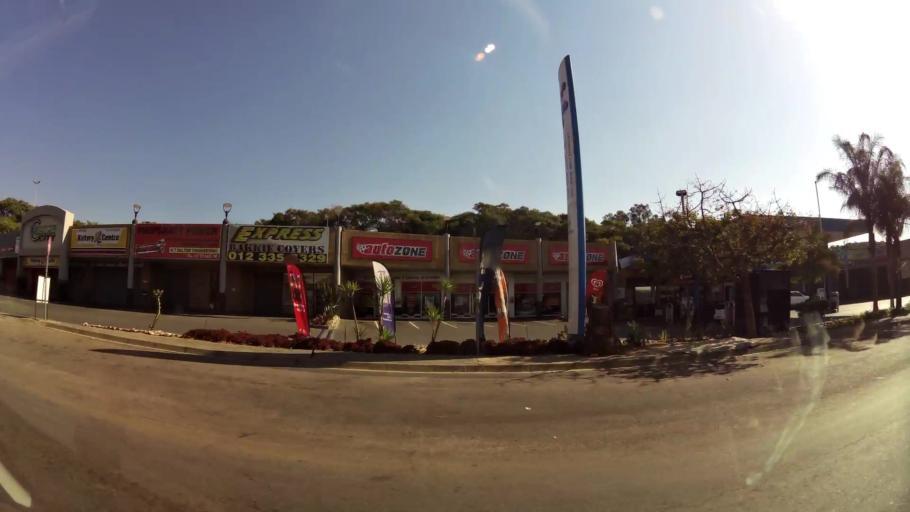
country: ZA
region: Gauteng
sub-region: City of Tshwane Metropolitan Municipality
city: Pretoria
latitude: -25.7194
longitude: 28.2026
